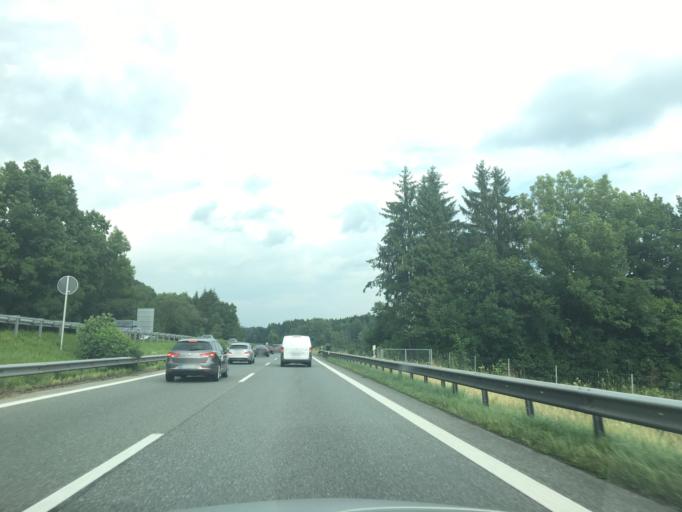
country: DE
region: Bavaria
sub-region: Upper Bavaria
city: Frasdorf
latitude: 47.7980
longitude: 12.2405
